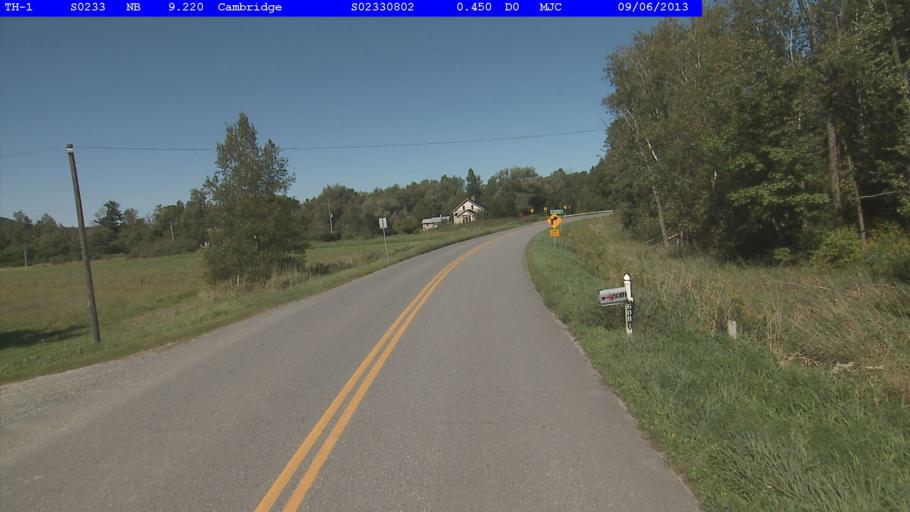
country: US
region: Vermont
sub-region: Chittenden County
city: Jericho
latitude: 44.5913
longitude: -72.8634
